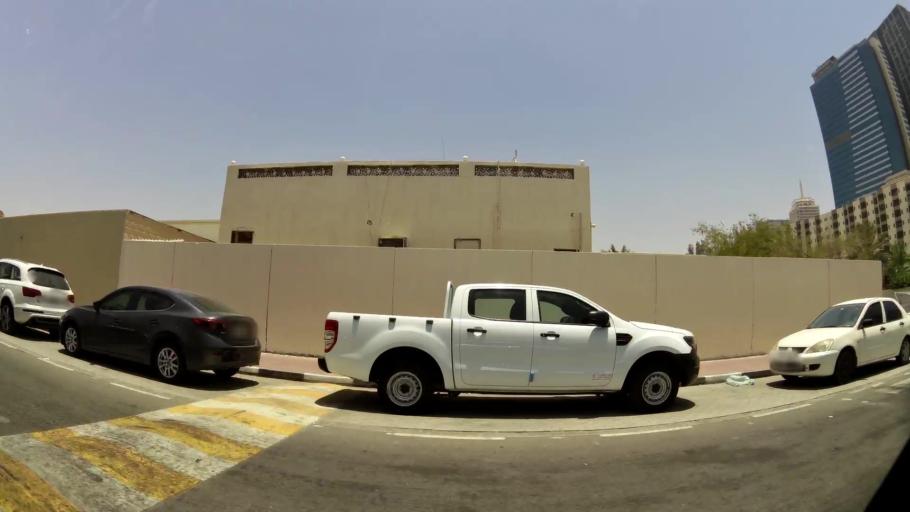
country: AE
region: Ash Shariqah
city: Sharjah
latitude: 25.2331
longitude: 55.2864
